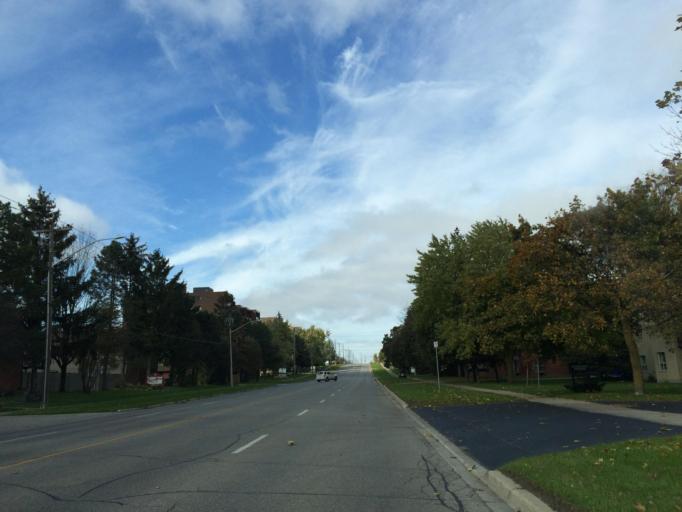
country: CA
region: Ontario
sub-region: Wellington County
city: Guelph
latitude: 43.5359
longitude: -80.2746
